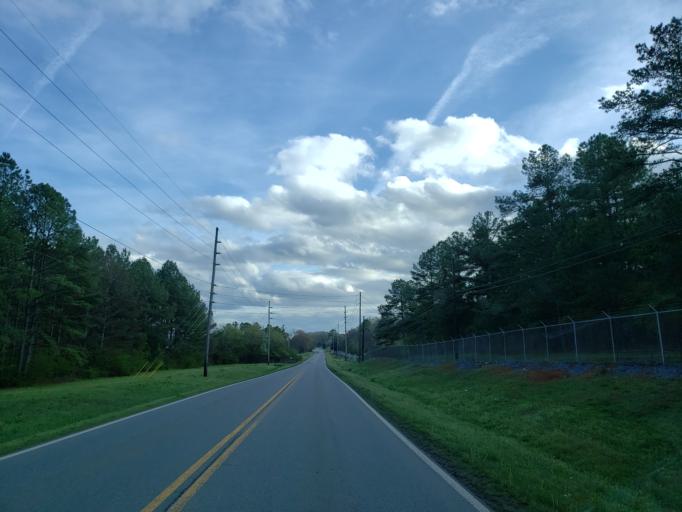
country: US
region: Georgia
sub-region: Bartow County
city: Cartersville
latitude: 34.2342
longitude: -84.8052
